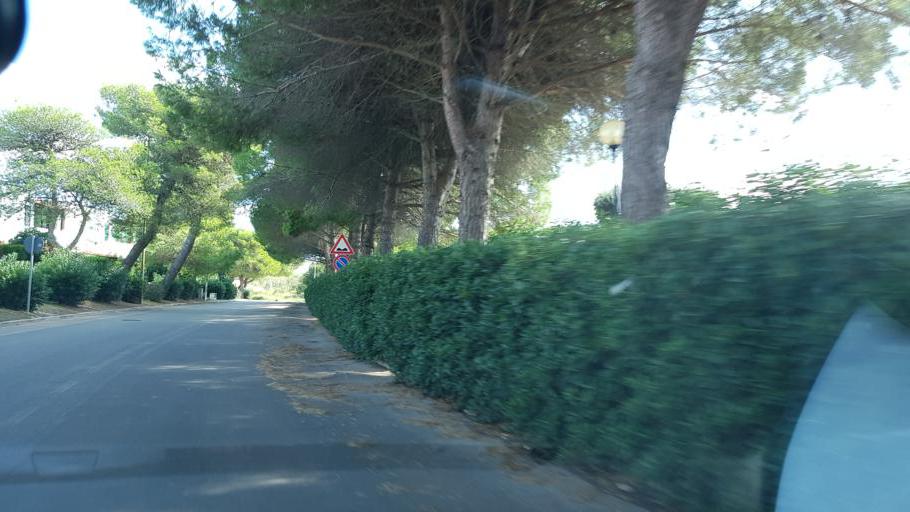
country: IT
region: Apulia
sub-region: Provincia di Lecce
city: Borgagne
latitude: 40.2716
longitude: 18.4252
